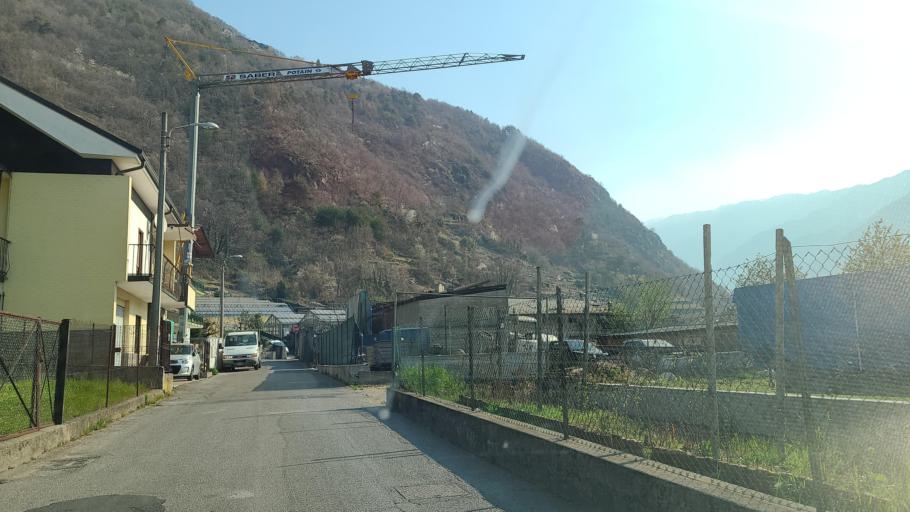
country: IT
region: Lombardy
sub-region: Provincia di Sondrio
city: Tirano
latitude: 46.2212
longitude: 10.1560
